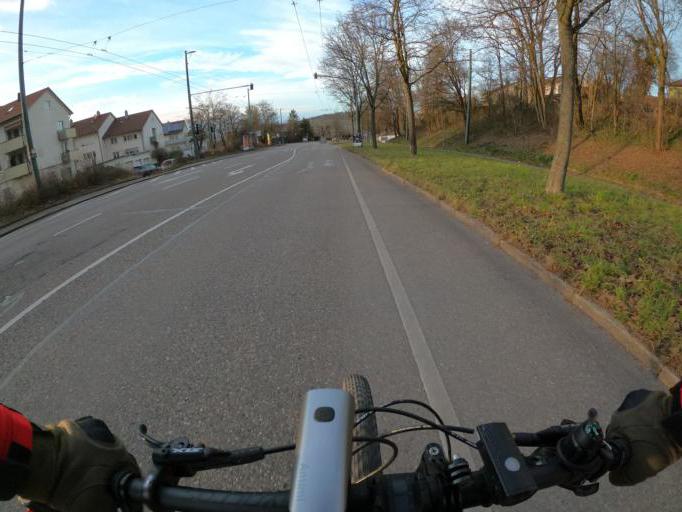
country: DE
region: Baden-Wuerttemberg
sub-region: Regierungsbezirk Stuttgart
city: Esslingen
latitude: 48.7279
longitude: 9.3008
